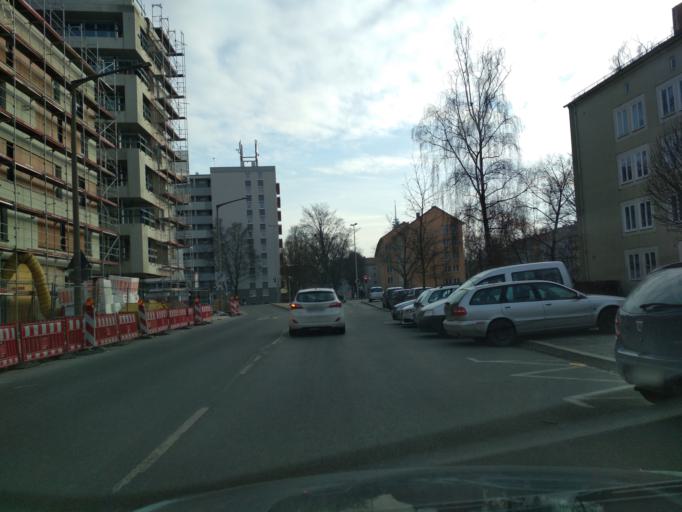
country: DE
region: Bavaria
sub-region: Regierungsbezirk Mittelfranken
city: Grossreuth bei Schweinau
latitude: 49.4431
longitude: 11.0453
